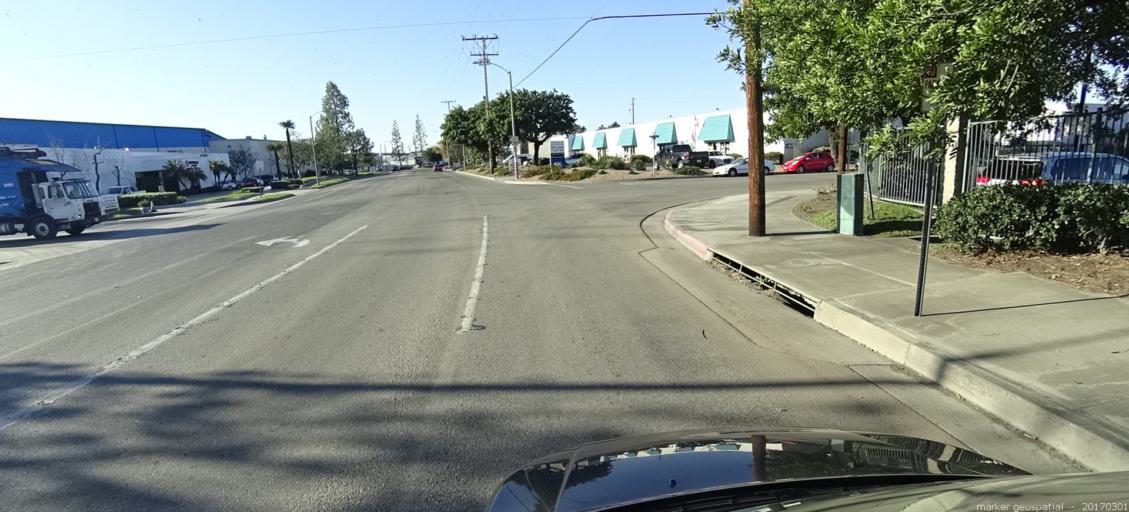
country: US
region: California
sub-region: Orange County
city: Placentia
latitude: 33.8488
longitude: -117.8691
